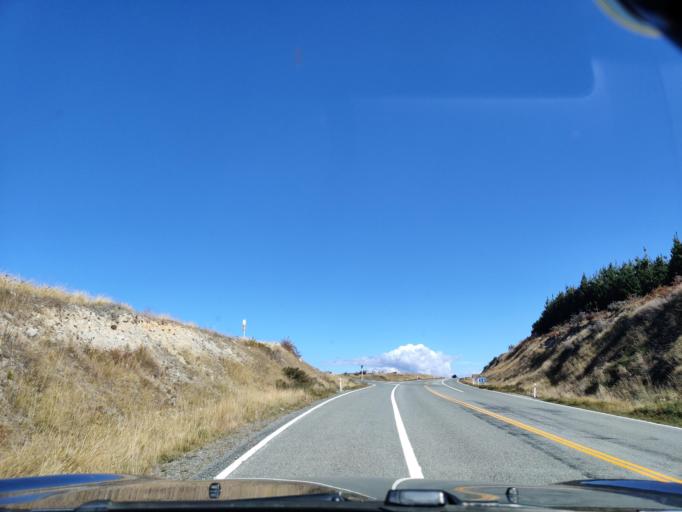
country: NZ
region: Canterbury
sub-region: Timaru District
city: Pleasant Point
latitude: -44.0886
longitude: 170.1353
